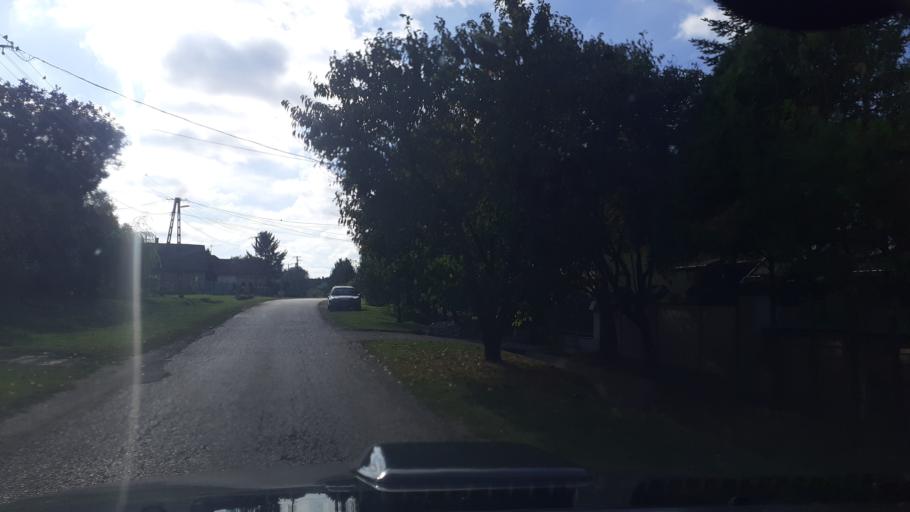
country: HU
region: Fejer
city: Baracs
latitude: 46.9230
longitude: 18.8754
